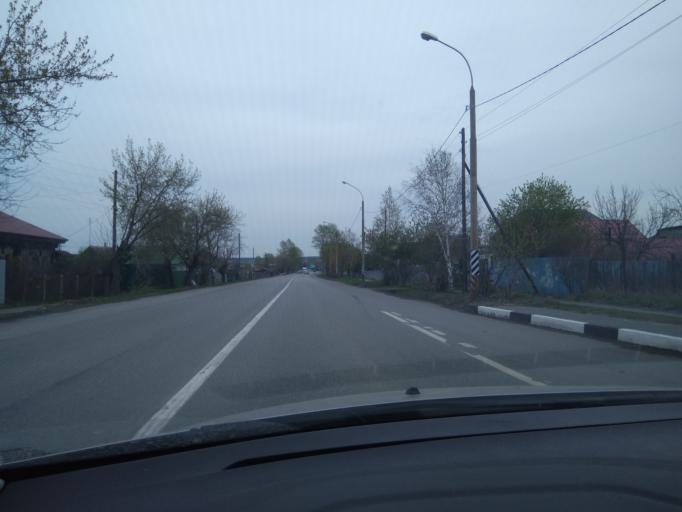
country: RU
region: Sverdlovsk
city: Beloyarskiy
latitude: 56.7566
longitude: 61.3775
